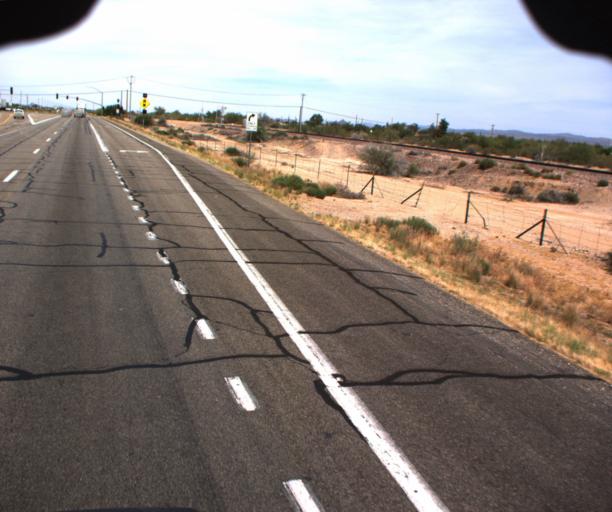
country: US
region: Arizona
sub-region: Maricopa County
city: Sun City West
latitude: 33.7771
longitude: -112.5274
